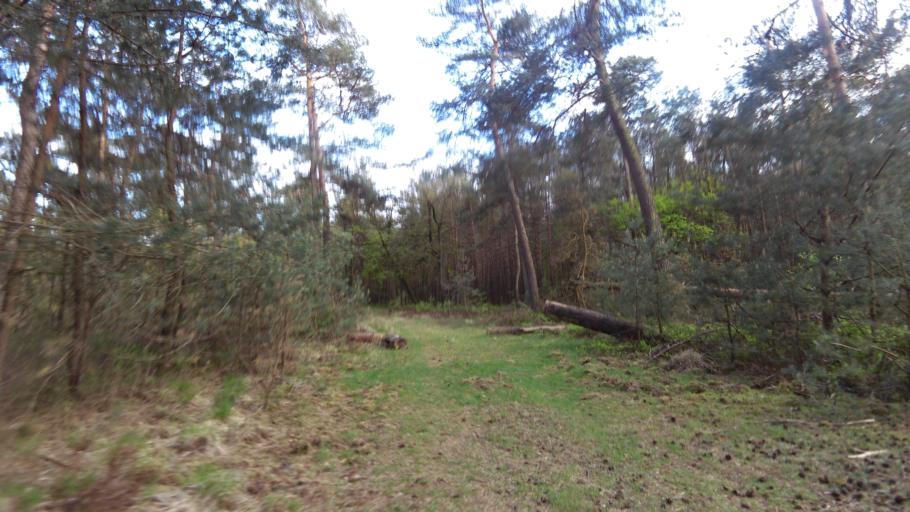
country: NL
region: Gelderland
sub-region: Gemeente Rozendaal
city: Rozendaal
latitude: 52.0275
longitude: 5.9554
